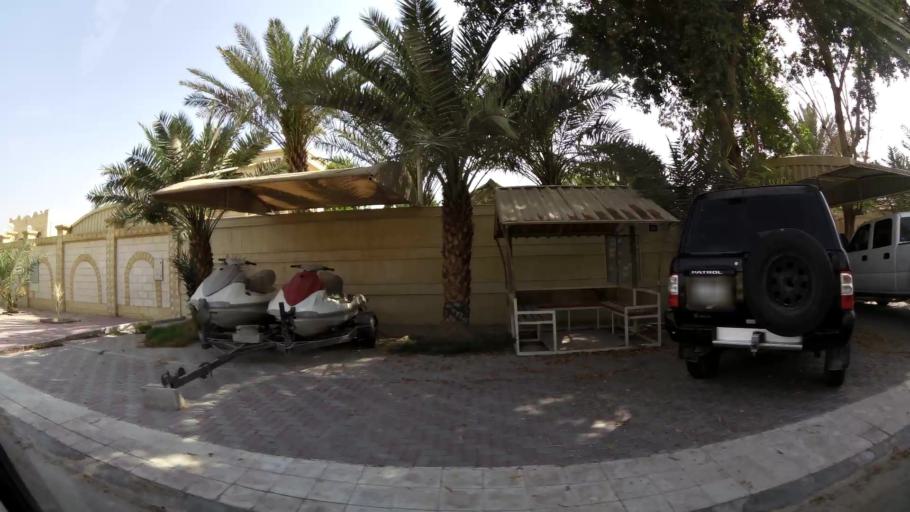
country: AE
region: Ash Shariqah
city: Sharjah
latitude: 25.2707
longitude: 55.4127
